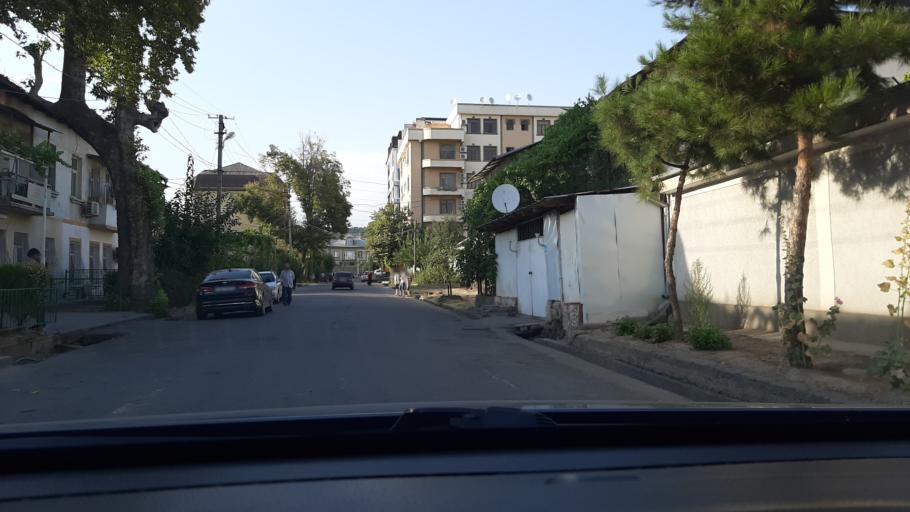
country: TJ
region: Dushanbe
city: Dushanbe
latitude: 38.5656
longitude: 68.8118
